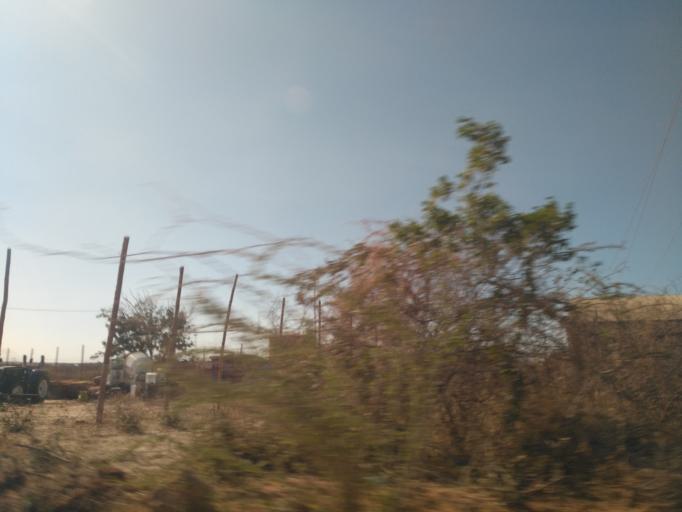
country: TZ
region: Dodoma
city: Dodoma
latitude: -6.1815
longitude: 35.6976
